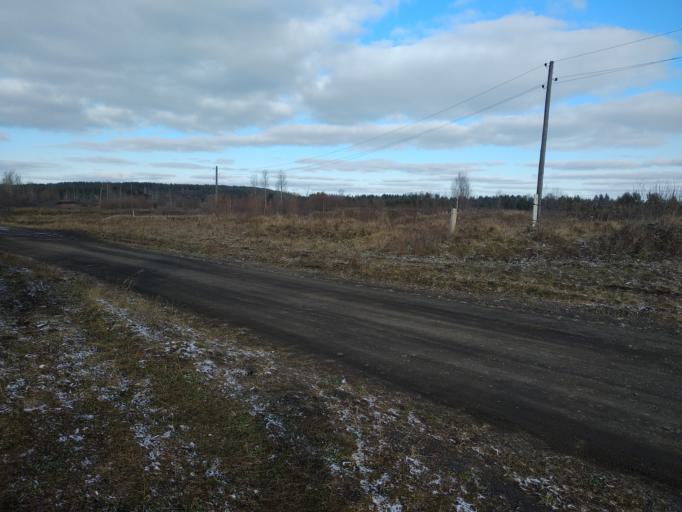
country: RU
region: Sverdlovsk
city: Karpinsk
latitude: 59.7593
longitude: 59.9404
